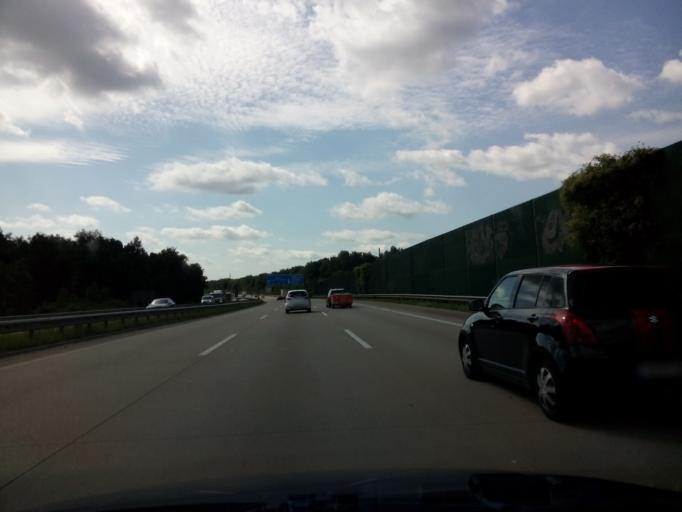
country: DE
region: Lower Saxony
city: Ritterhude
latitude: 53.1572
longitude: 8.7230
